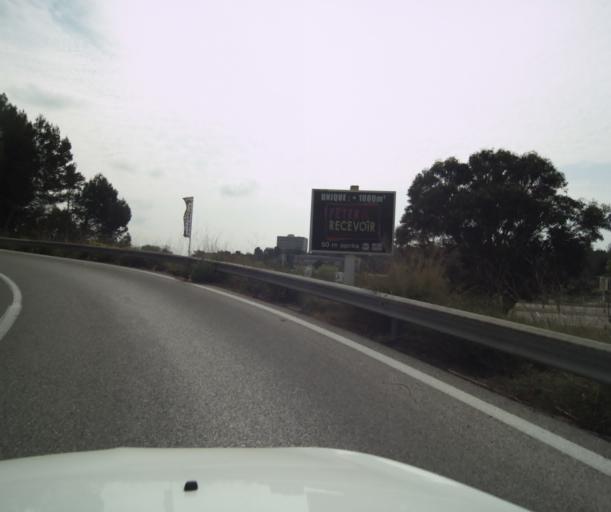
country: FR
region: Provence-Alpes-Cote d'Azur
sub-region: Departement du Var
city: La Garde
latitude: 43.1388
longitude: 6.0146
